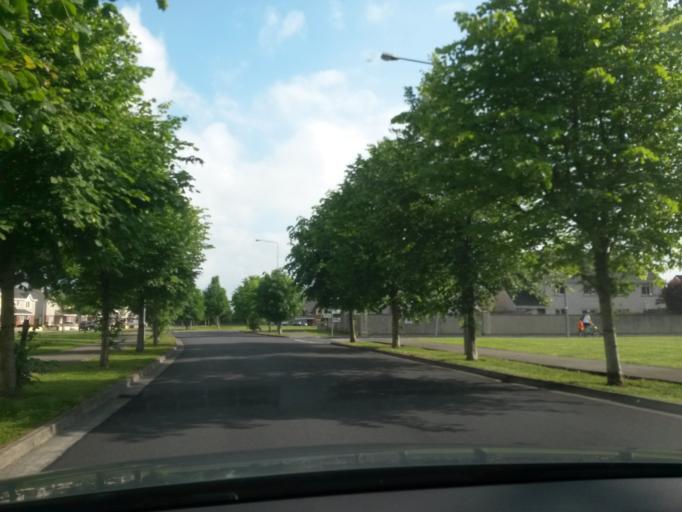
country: IE
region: Munster
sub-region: An Clar
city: Ennis
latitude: 52.8382
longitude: -8.9617
